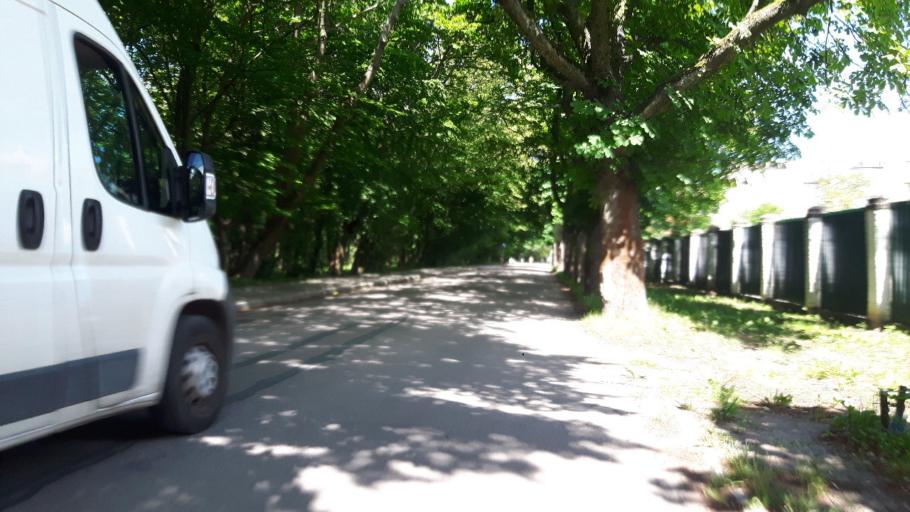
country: RU
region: Kaliningrad
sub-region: Zelenogradskiy Rayon
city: Zelenogradsk
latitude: 54.9623
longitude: 20.4900
